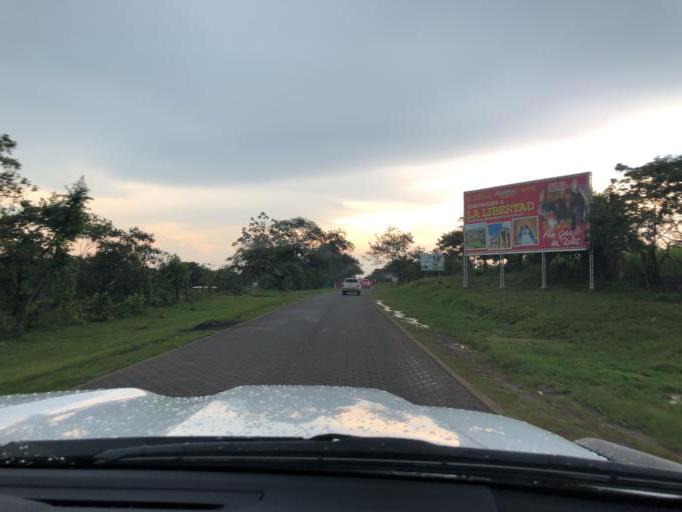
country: NI
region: Chontales
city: La Libertad
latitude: 12.2106
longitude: -85.1791
